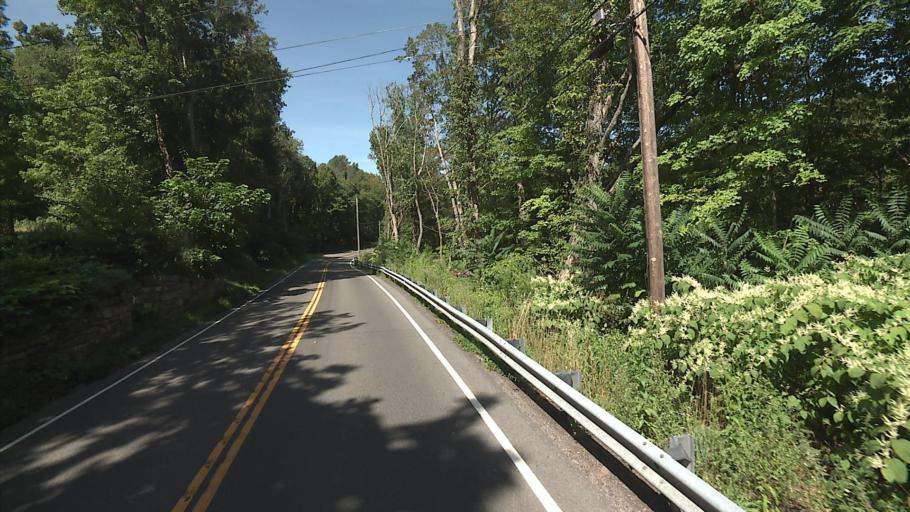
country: US
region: Connecticut
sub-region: New Haven County
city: Southbury
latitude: 41.4563
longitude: -73.1661
